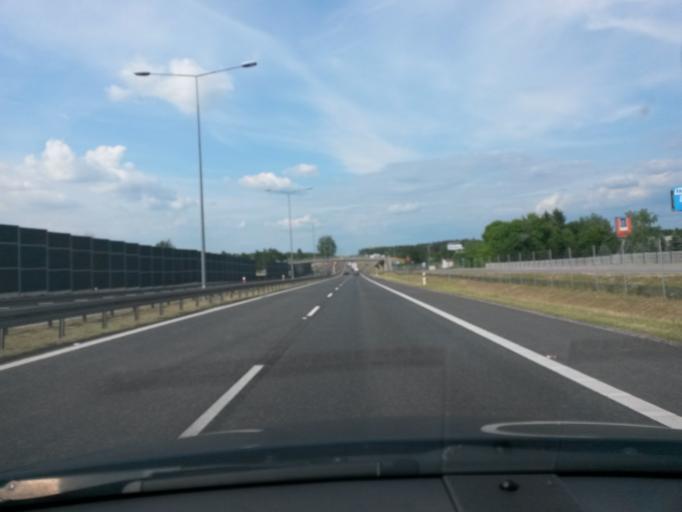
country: PL
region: Masovian Voivodeship
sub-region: Powiat zyrardowski
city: Mszczonow
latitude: 51.9391
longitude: 20.4799
